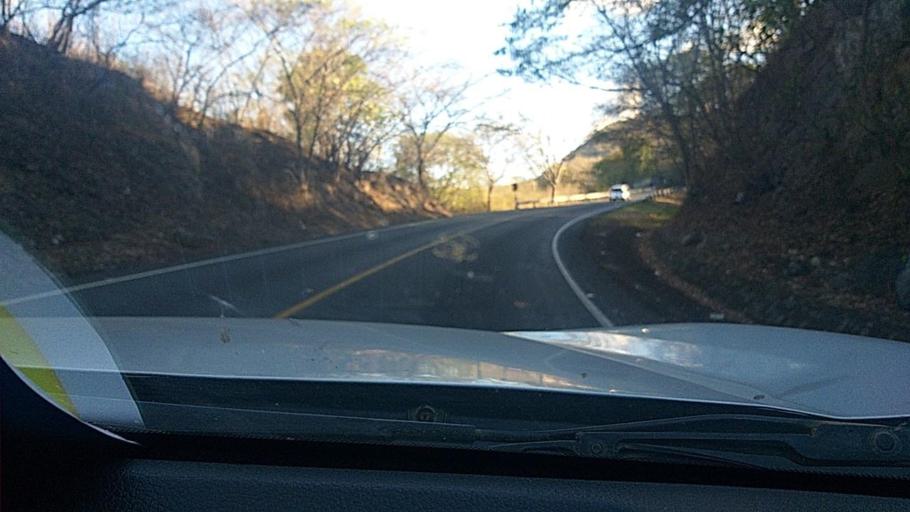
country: NI
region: Esteli
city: Condega
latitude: 13.2644
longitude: -86.3541
